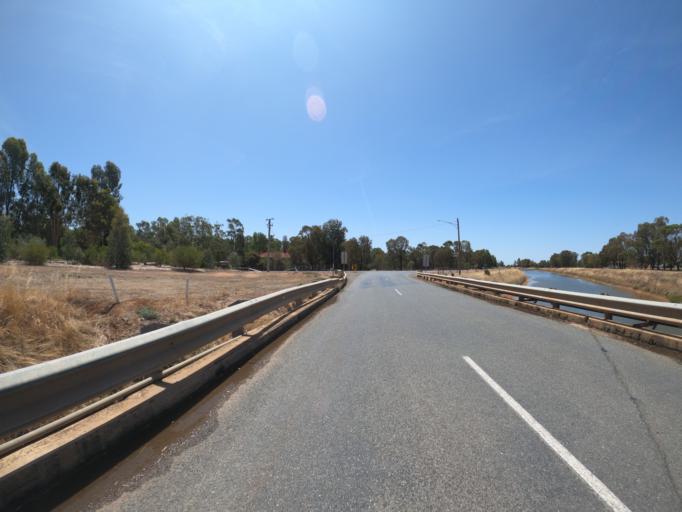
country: AU
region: Victoria
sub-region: Moira
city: Yarrawonga
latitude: -36.0172
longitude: 145.9955
